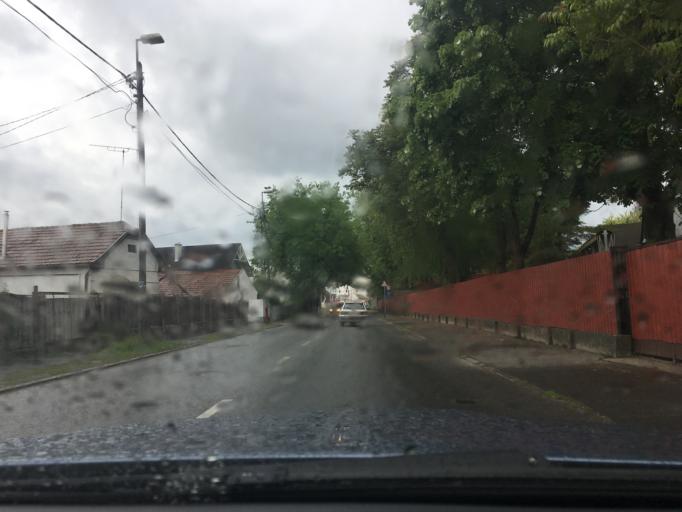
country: HU
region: Hajdu-Bihar
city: Debrecen
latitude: 47.5213
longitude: 21.6590
